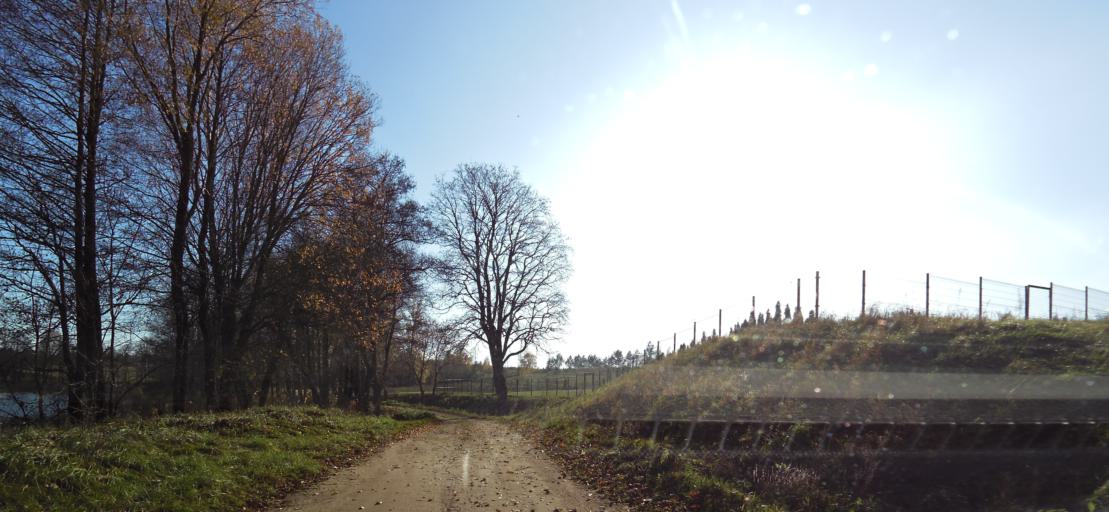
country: LT
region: Vilnius County
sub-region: Vilniaus Rajonas
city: Vievis
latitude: 54.6450
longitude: 24.7443
